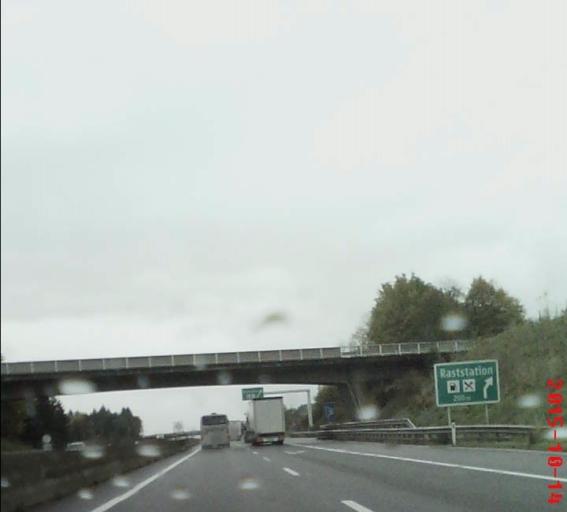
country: AT
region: Upper Austria
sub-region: Wels-Land
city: Bachmanning
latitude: 48.1782
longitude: 13.7581
